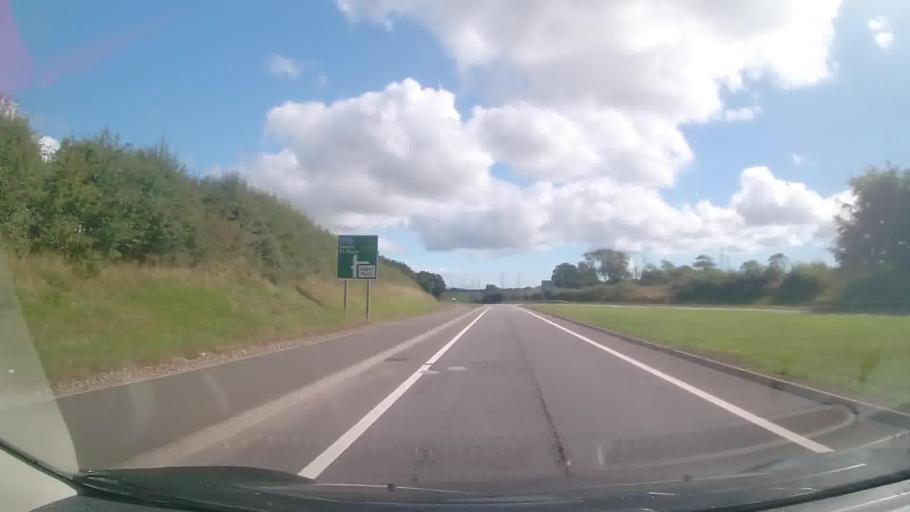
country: GB
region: Wales
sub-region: Pembrokeshire
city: Pembroke
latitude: 51.6891
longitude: -4.8663
